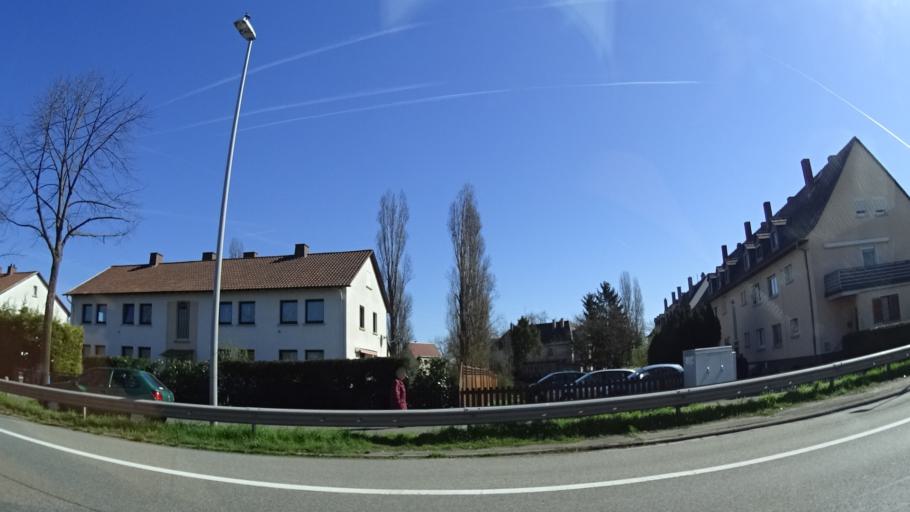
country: DE
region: Rheinland-Pfalz
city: Osthofen
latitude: 49.6930
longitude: 8.3519
